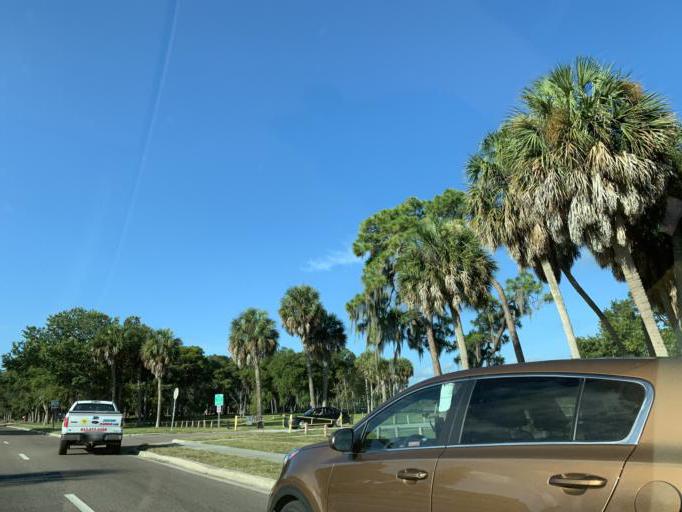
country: US
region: Florida
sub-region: Pinellas County
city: Saint Petersburg
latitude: 27.7353
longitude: -82.6466
